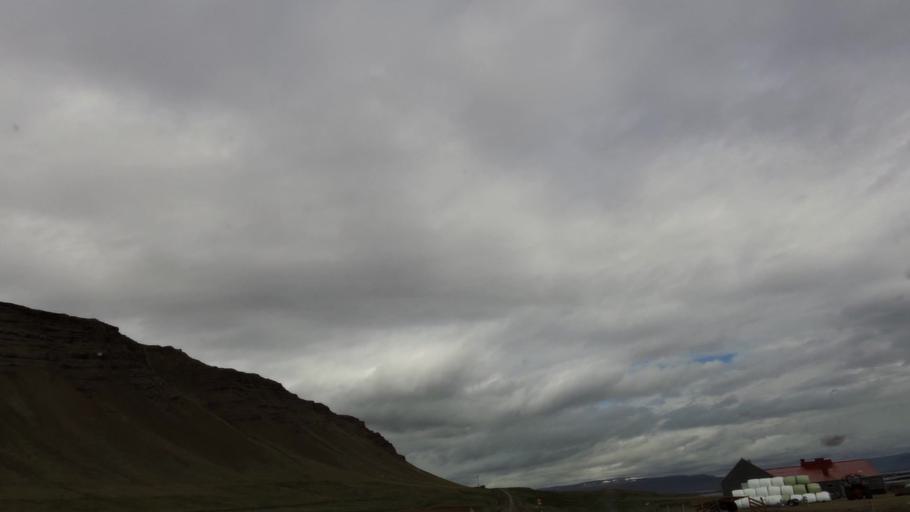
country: IS
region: West
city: Stykkisholmur
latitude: 65.4553
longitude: -22.2003
